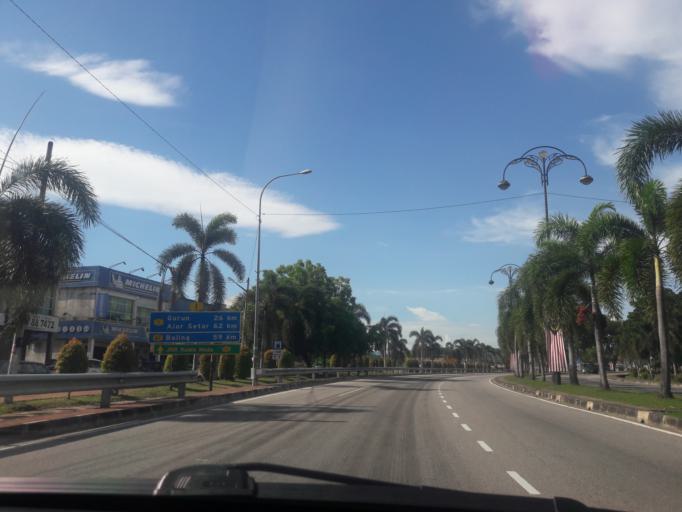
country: MY
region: Kedah
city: Sungai Petani
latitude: 5.6172
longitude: 100.4728
